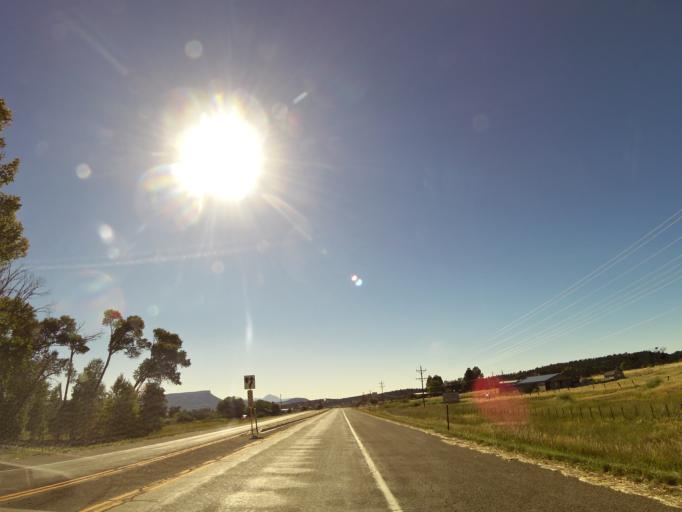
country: US
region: Colorado
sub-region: Montezuma County
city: Mancos
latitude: 37.3477
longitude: -108.2805
